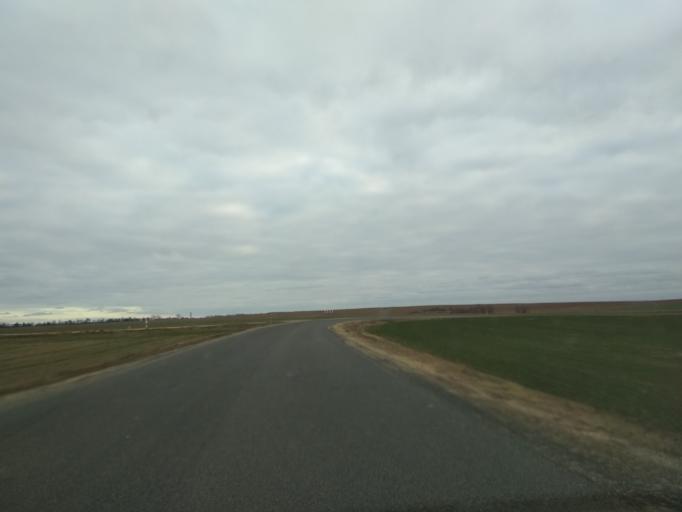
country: BY
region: Minsk
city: Mar''ina Horka
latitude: 53.5503
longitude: 28.1302
